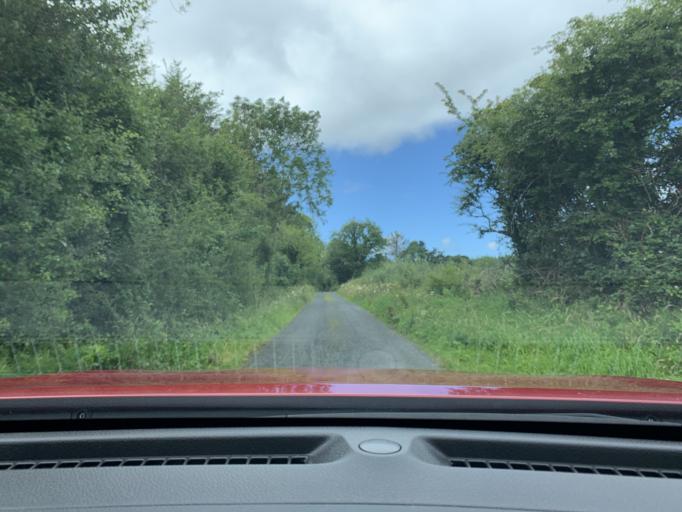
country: IE
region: Connaught
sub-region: Sligo
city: Sligo
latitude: 54.3316
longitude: -8.4913
